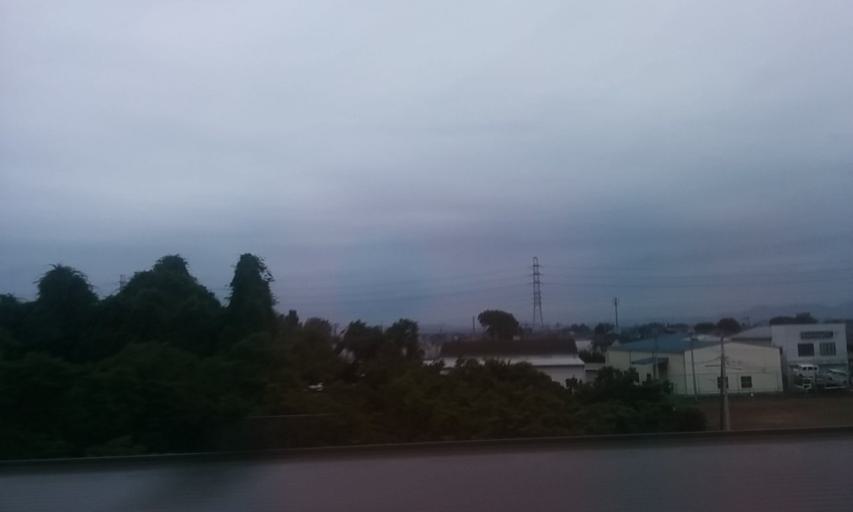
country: JP
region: Tochigi
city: Oyama
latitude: 36.2585
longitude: 139.7701
